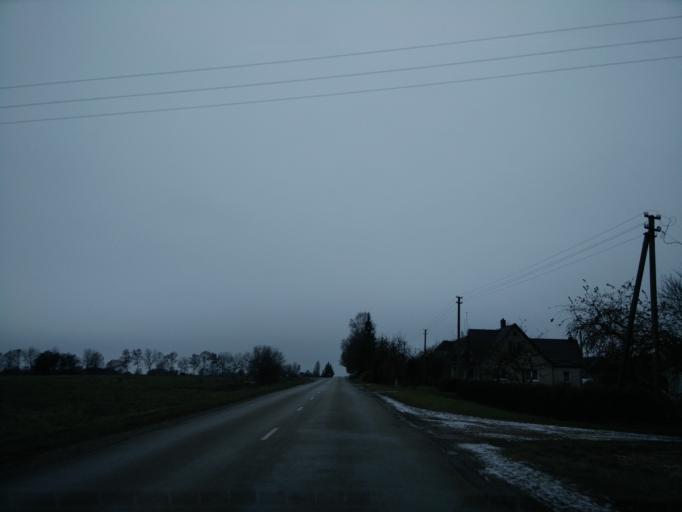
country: LT
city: Ariogala
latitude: 55.3253
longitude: 23.4243
